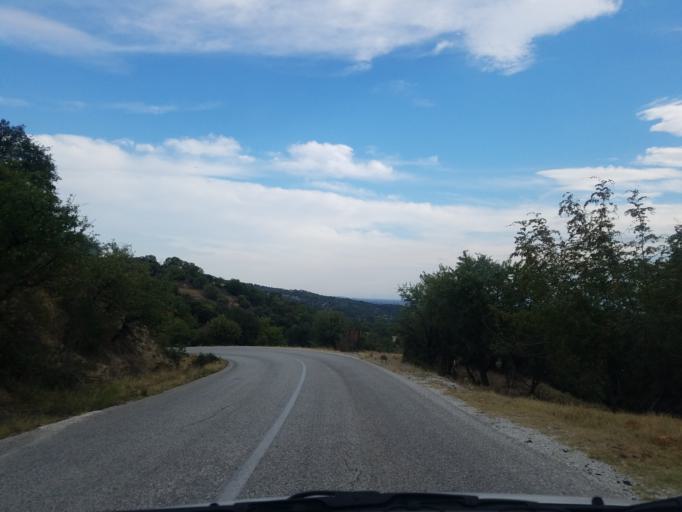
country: GR
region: Thessaly
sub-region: Trikala
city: Kalampaka
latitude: 39.7018
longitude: 21.6483
